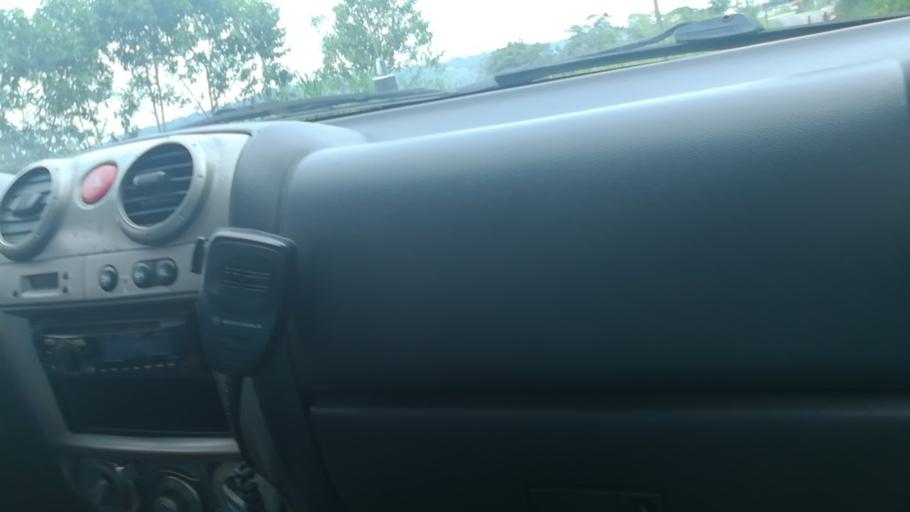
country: EC
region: Napo
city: Tena
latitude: -0.9770
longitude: -77.8153
